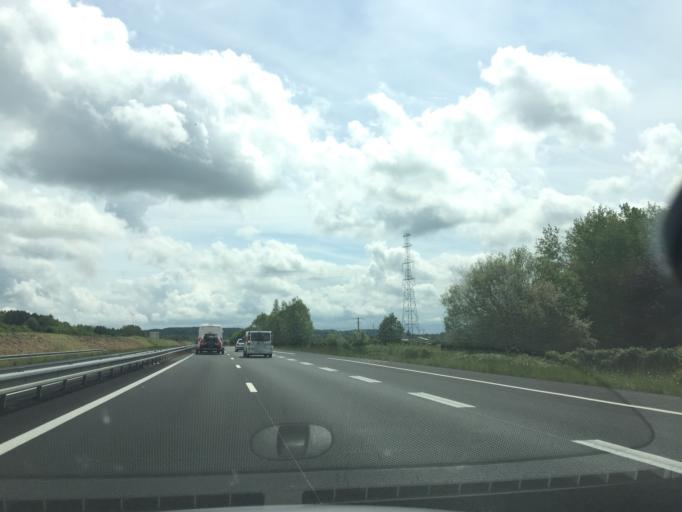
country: FR
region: Pays de la Loire
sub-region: Departement de la Sarthe
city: Teloche
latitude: 47.8791
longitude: 0.3038
